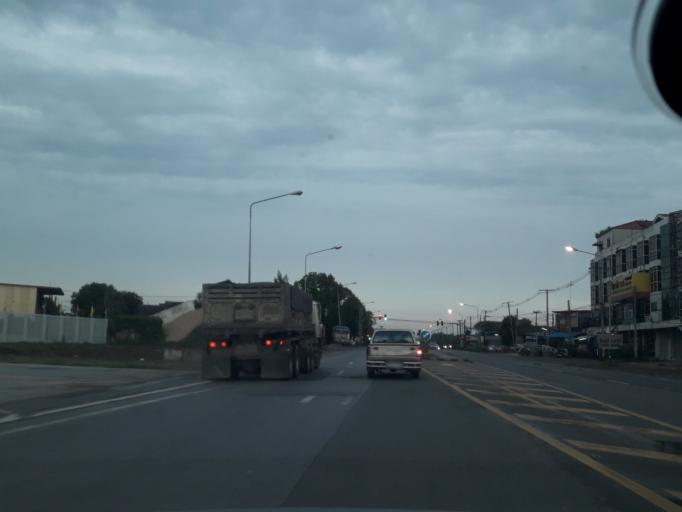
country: TH
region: Pathum Thani
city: Ban Rangsit
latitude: 14.0442
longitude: 100.7491
